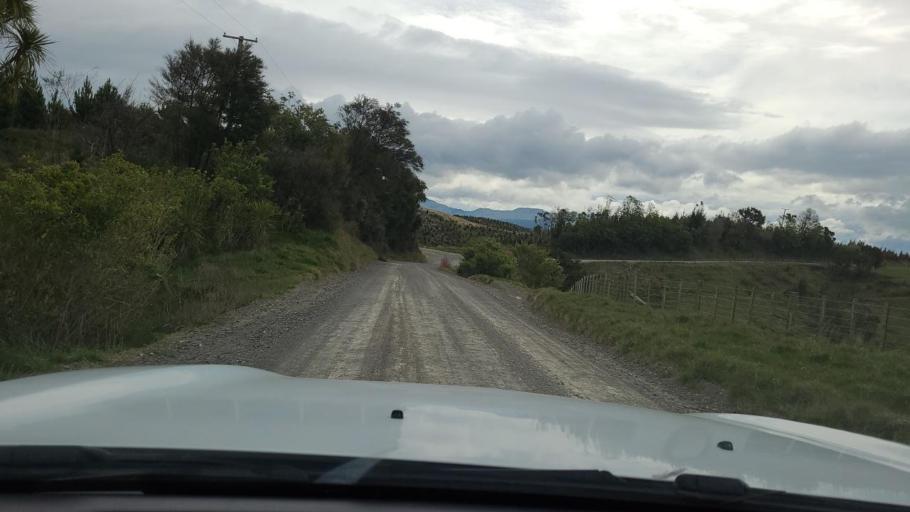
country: NZ
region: Hawke's Bay
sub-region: Napier City
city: Napier
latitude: -39.3374
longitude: 176.8301
